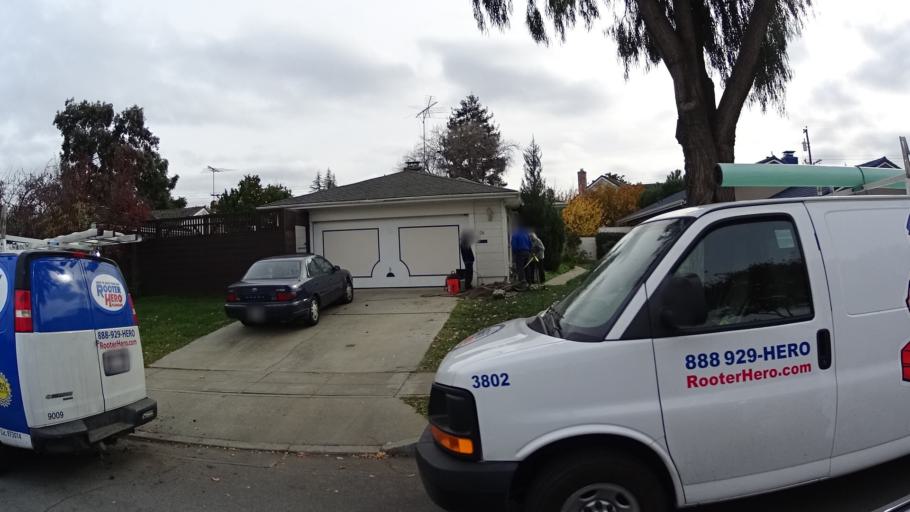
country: US
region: California
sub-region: Santa Clara County
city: Sunnyvale
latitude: 37.3650
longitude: -122.0481
